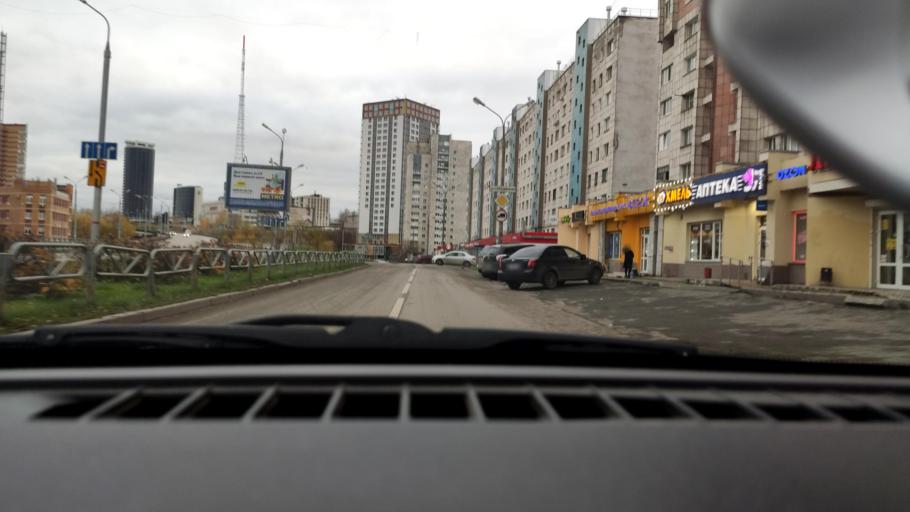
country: RU
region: Perm
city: Perm
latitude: 58.0045
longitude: 56.2773
